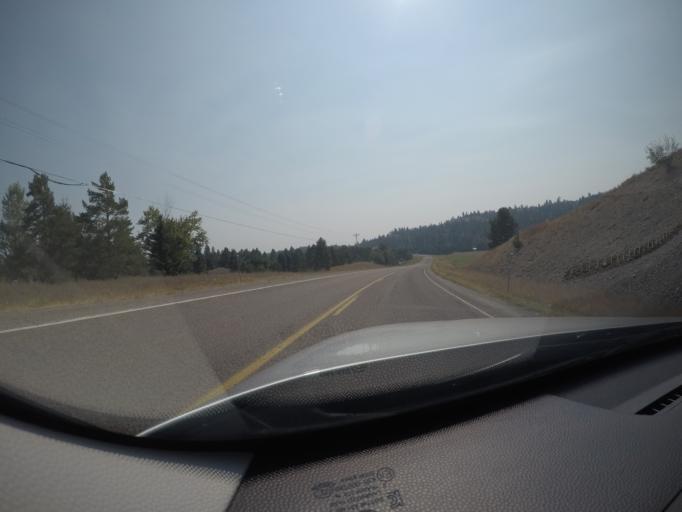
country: US
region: Montana
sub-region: Lake County
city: Polson
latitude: 47.7604
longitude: -114.1647
